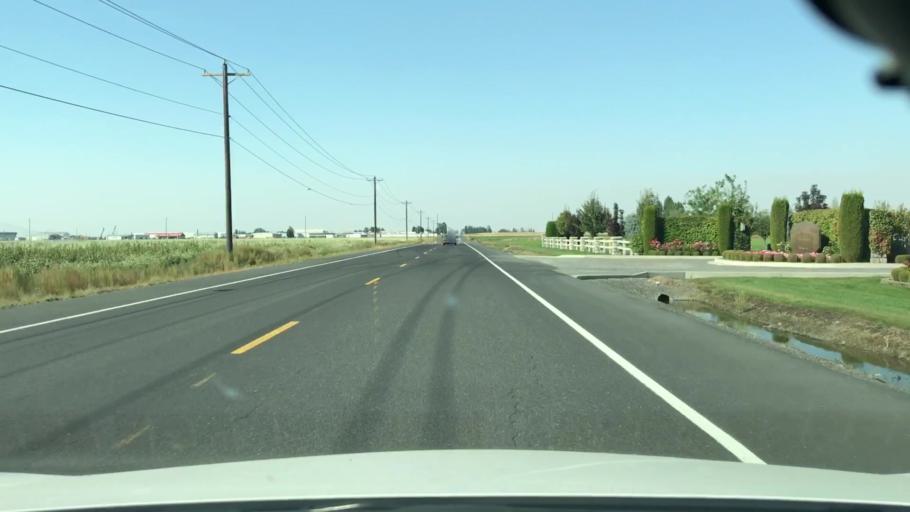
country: US
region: Washington
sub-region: Grant County
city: Moses Lake
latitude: 47.1247
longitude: -119.2358
